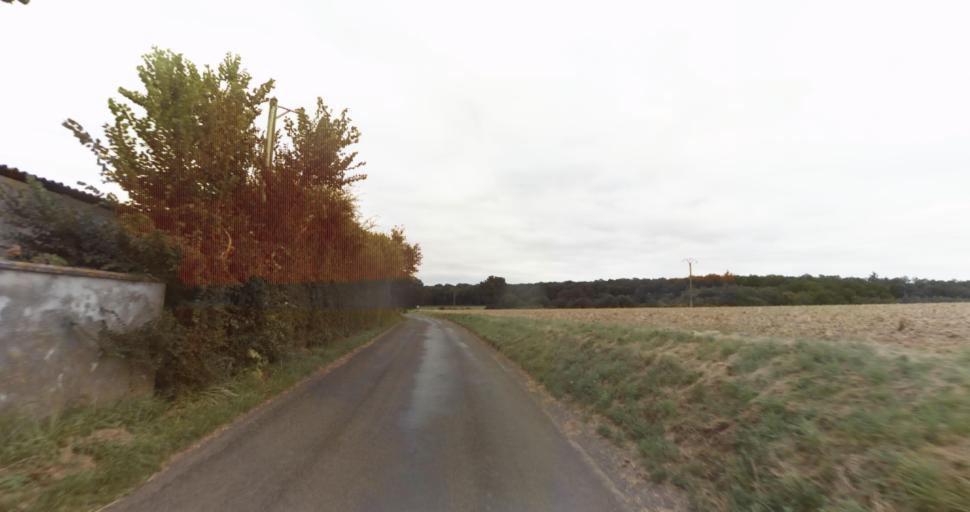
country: FR
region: Haute-Normandie
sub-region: Departement de l'Eure
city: Marcilly-sur-Eure
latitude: 48.8806
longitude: 1.3112
